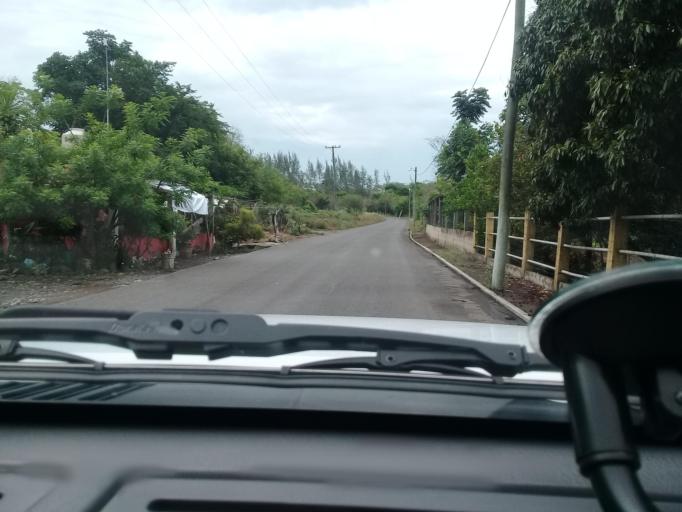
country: MX
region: Veracruz
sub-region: Paso de Ovejas
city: El Hatito
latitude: 19.3156
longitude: -96.3743
